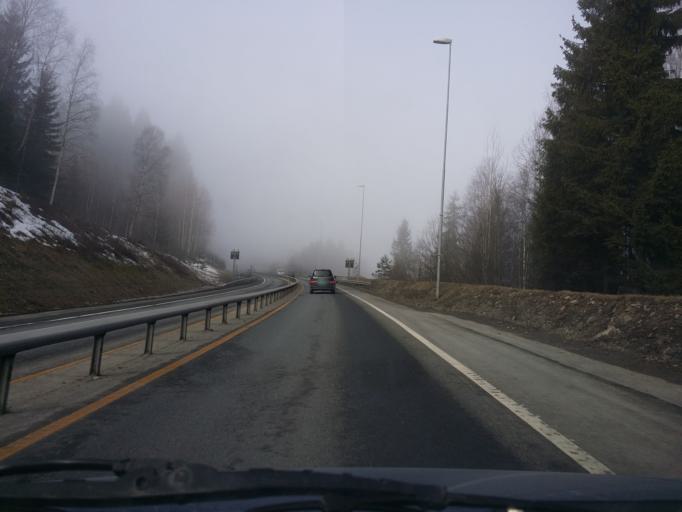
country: NO
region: Buskerud
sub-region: Drammen
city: Drammen
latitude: 59.7398
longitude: 10.1476
